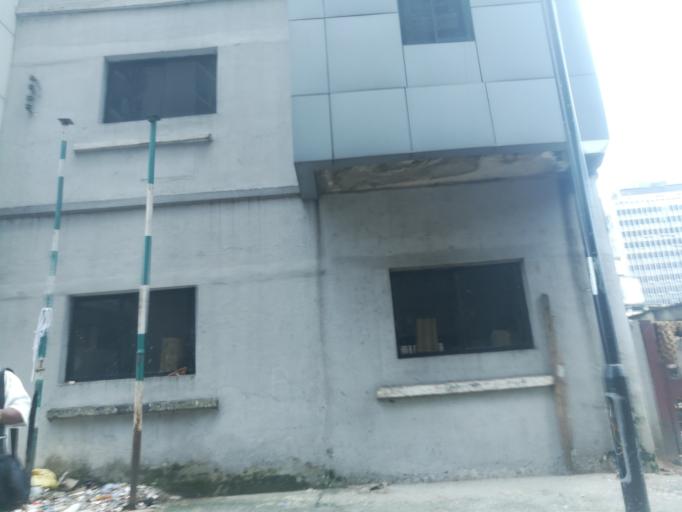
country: NG
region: Lagos
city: Lagos
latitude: 6.4529
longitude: 3.3892
